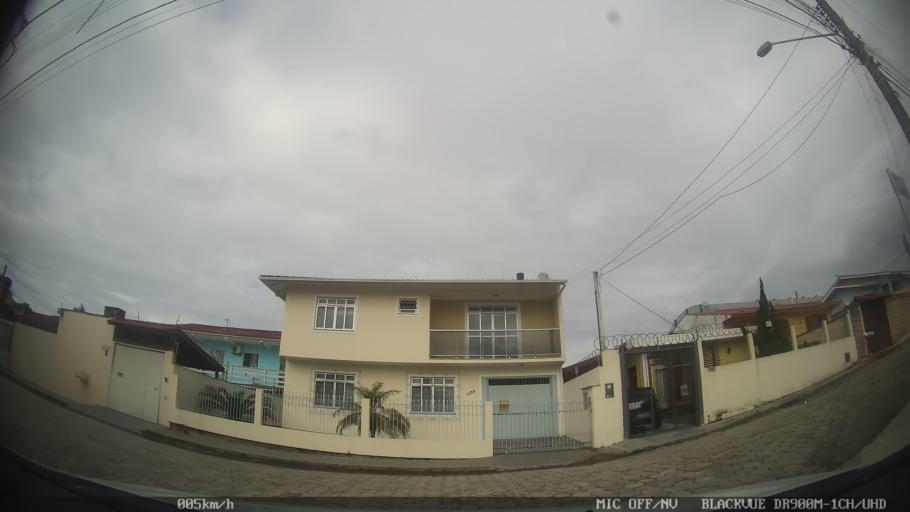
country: BR
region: Santa Catarina
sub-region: Sao Jose
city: Campinas
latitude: -27.5590
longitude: -48.6259
